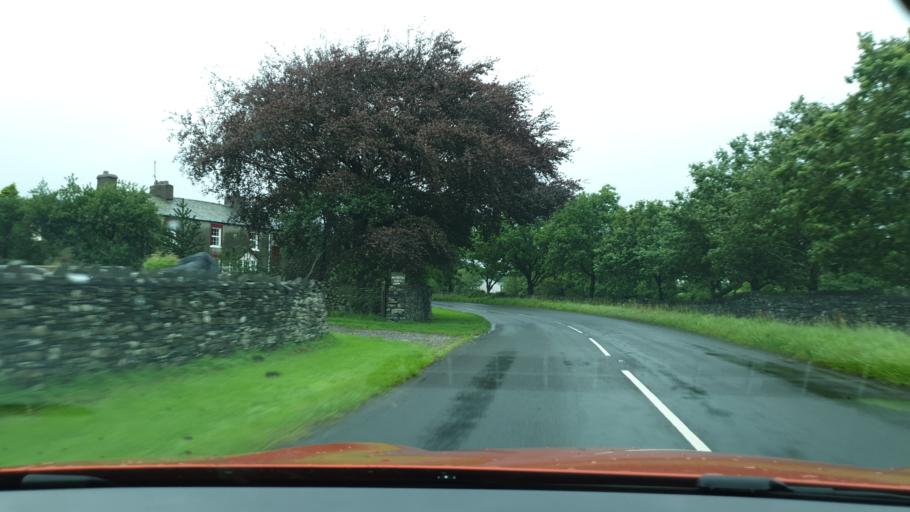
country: GB
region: England
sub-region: Cumbria
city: Ulverston
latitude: 54.2675
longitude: -3.0853
